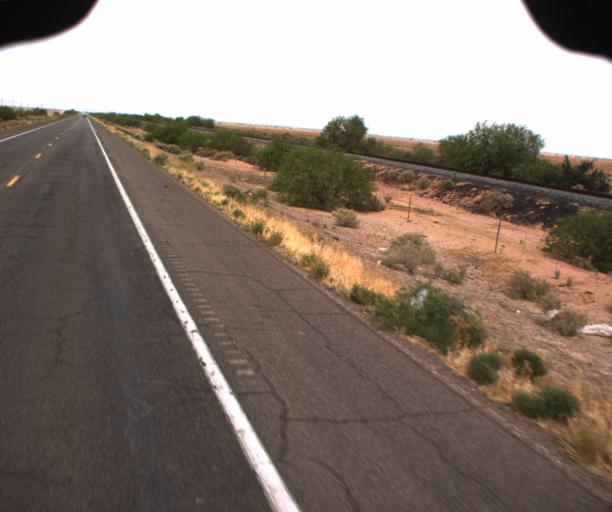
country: US
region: Arizona
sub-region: Pinal County
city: Sacaton
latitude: 33.1541
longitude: -111.7739
